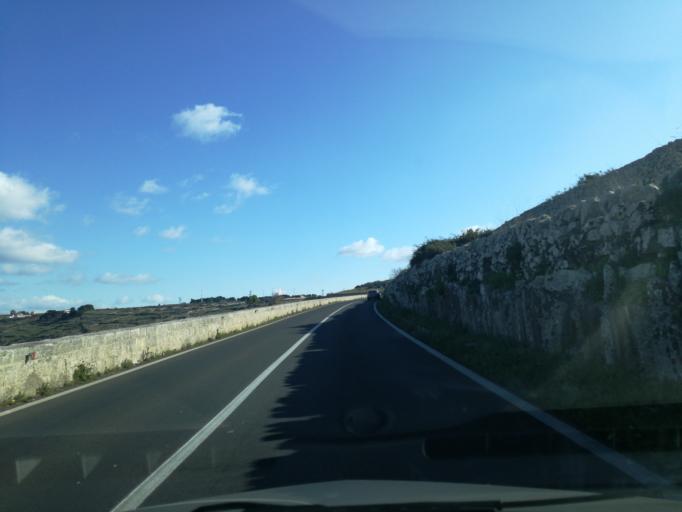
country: IT
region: Sicily
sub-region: Ragusa
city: Comiso
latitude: 36.9412
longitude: 14.6385
